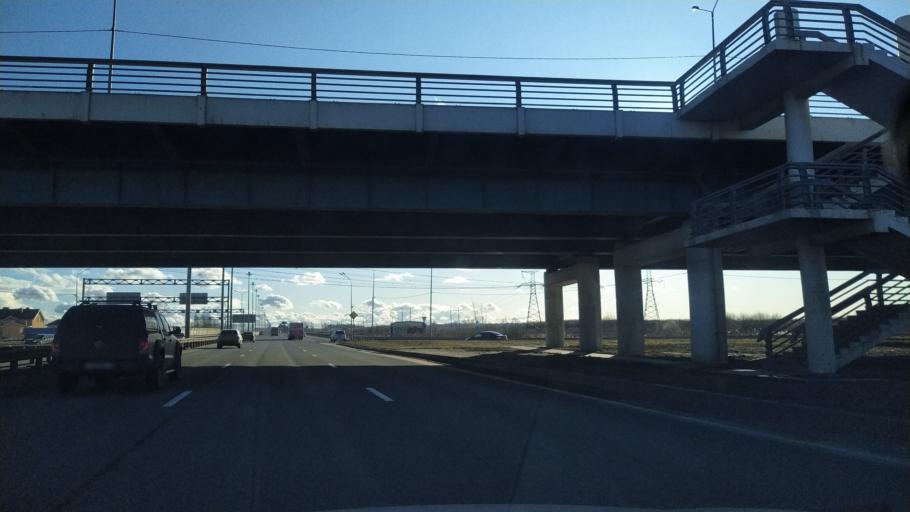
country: RU
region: St.-Petersburg
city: Aleksandrovskaya
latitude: 59.7448
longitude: 30.3099
